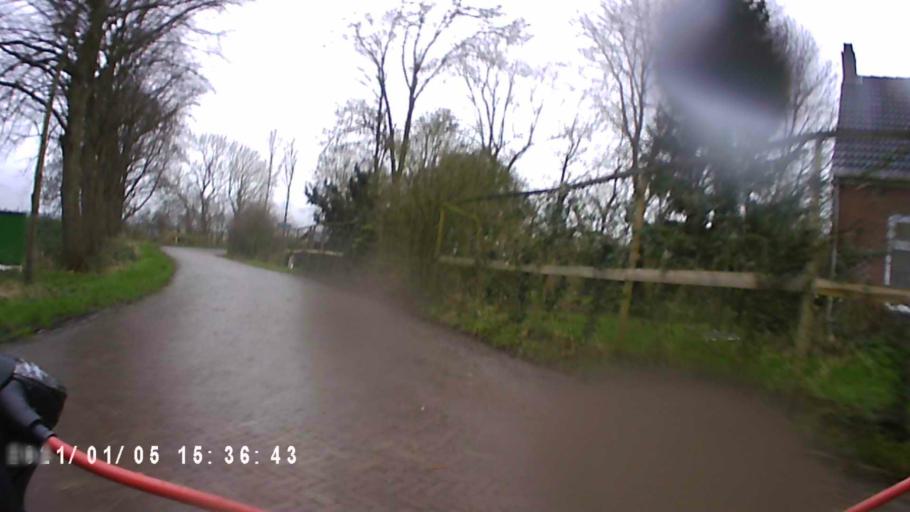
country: DE
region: Lower Saxony
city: Bunde
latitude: 53.2133
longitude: 7.1640
